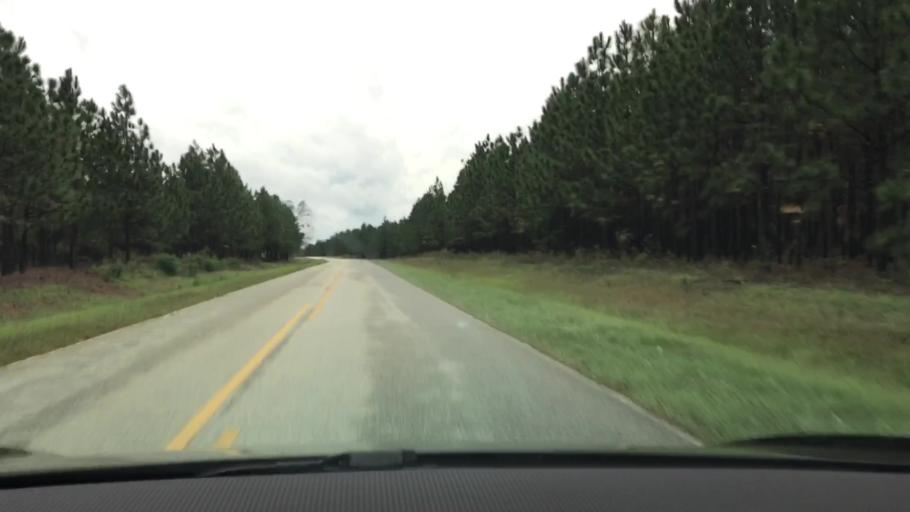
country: US
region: Georgia
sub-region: Jefferson County
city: Wadley
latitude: 32.8360
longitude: -82.3899
